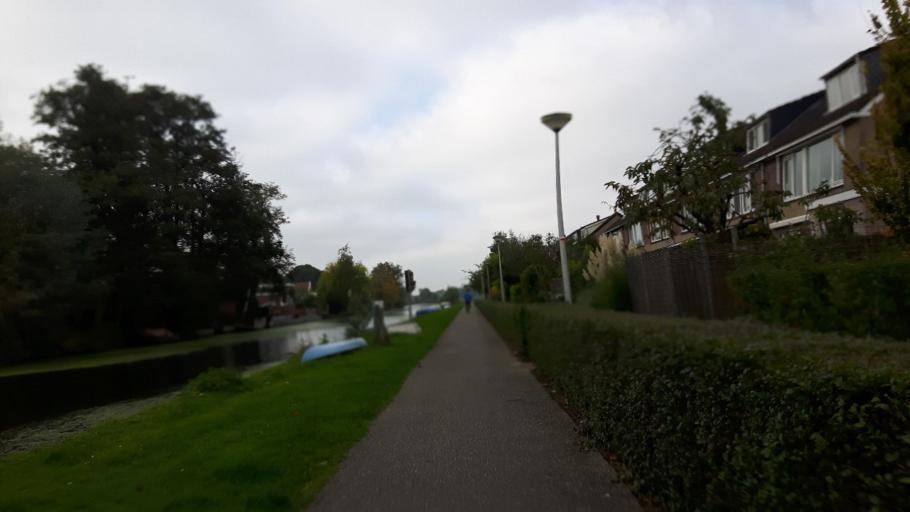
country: NL
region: South Holland
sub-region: Gemeente Vlist
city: Haastrecht
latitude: 52.0014
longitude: 4.7694
